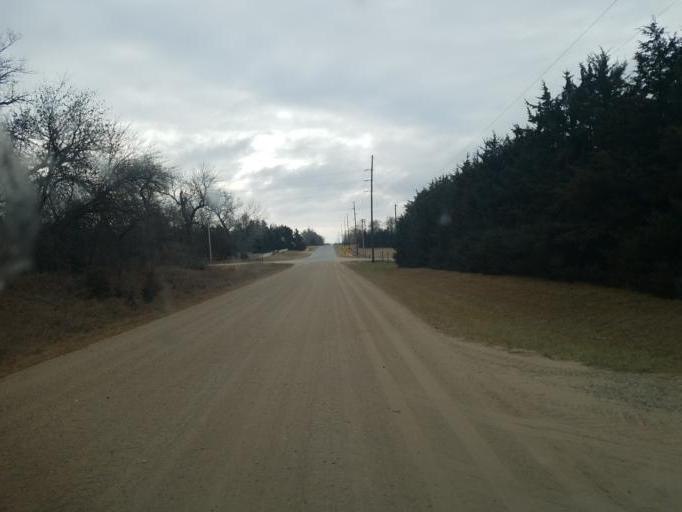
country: US
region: Nebraska
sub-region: Pierce County
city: Plainview
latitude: 42.3655
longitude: -97.7764
